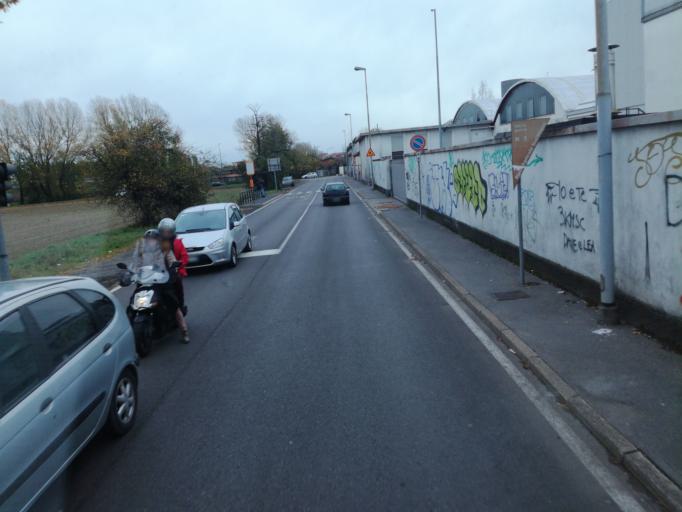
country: IT
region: Lombardy
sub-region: Citta metropolitana di Milano
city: Figino
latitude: 45.4730
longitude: 9.0766
